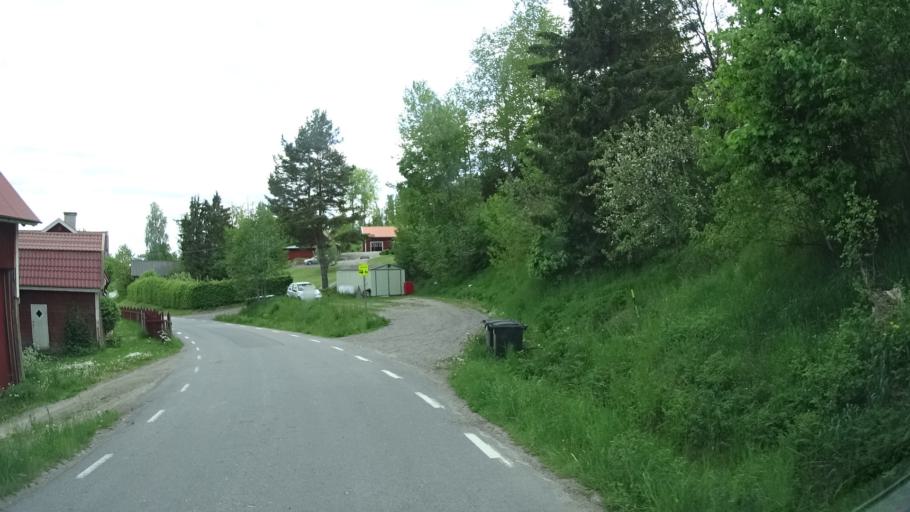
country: SE
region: OEstergoetland
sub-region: Finspangs Kommun
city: Finspang
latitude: 58.5902
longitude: 15.7741
